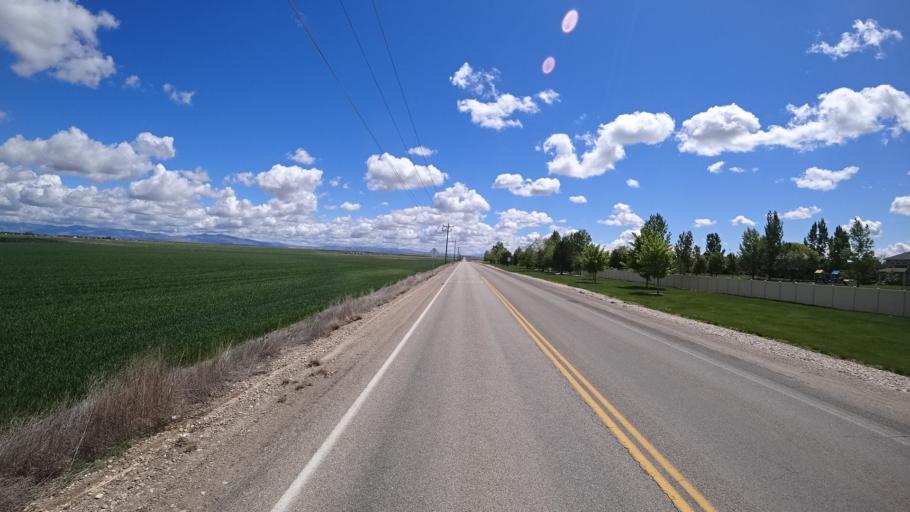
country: US
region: Idaho
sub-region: Ada County
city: Kuna
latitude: 43.4592
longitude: -116.3329
